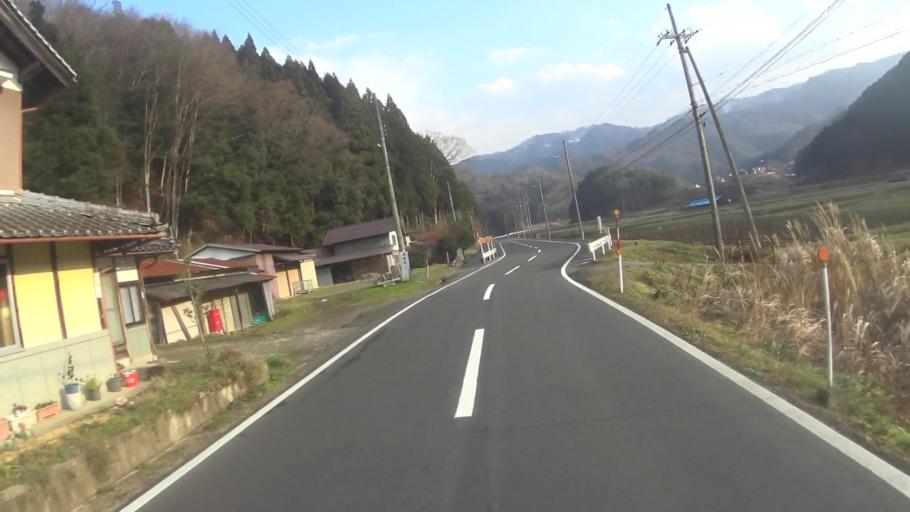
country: JP
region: Kyoto
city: Maizuru
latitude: 35.3684
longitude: 135.4294
